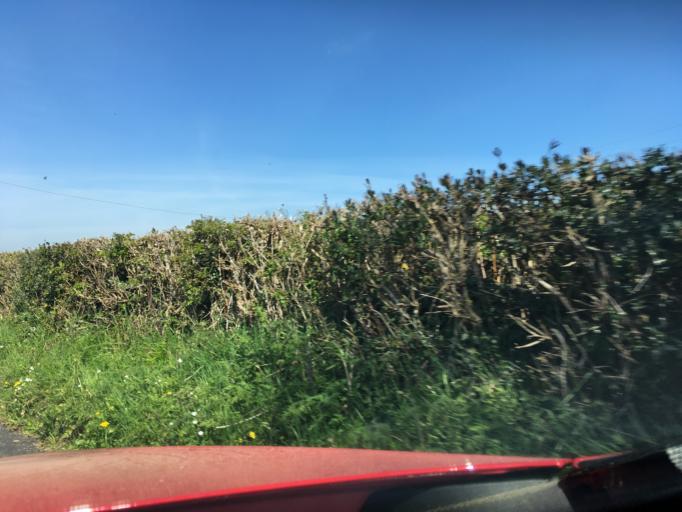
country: GB
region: Wales
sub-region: Monmouthshire
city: Llangwm
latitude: 51.7666
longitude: -2.8298
